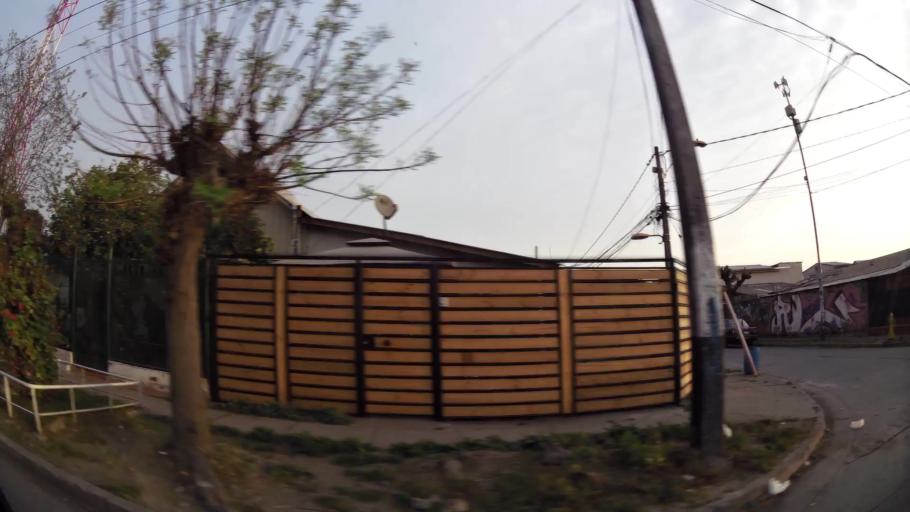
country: CL
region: Santiago Metropolitan
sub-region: Provincia de Santiago
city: Lo Prado
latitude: -33.5158
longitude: -70.7874
